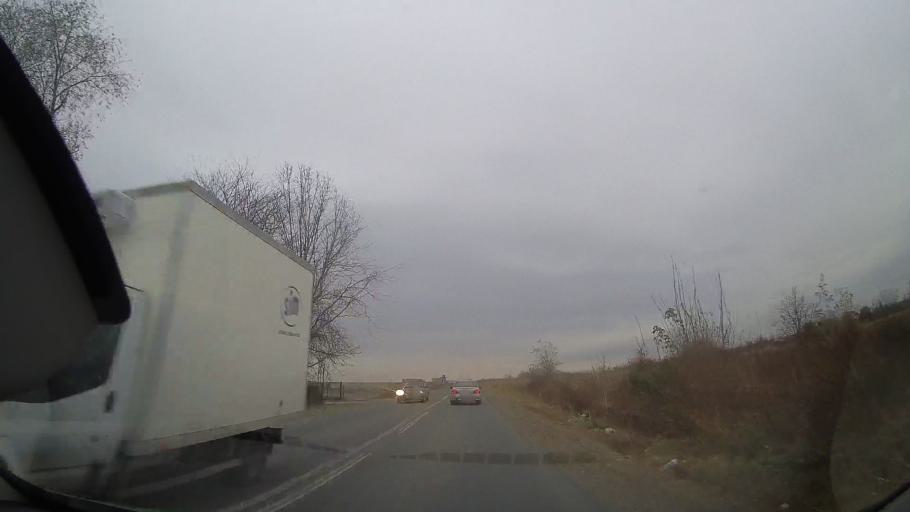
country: RO
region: Ialomita
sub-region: Oras Amara
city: Amara
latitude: 44.6220
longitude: 27.3014
